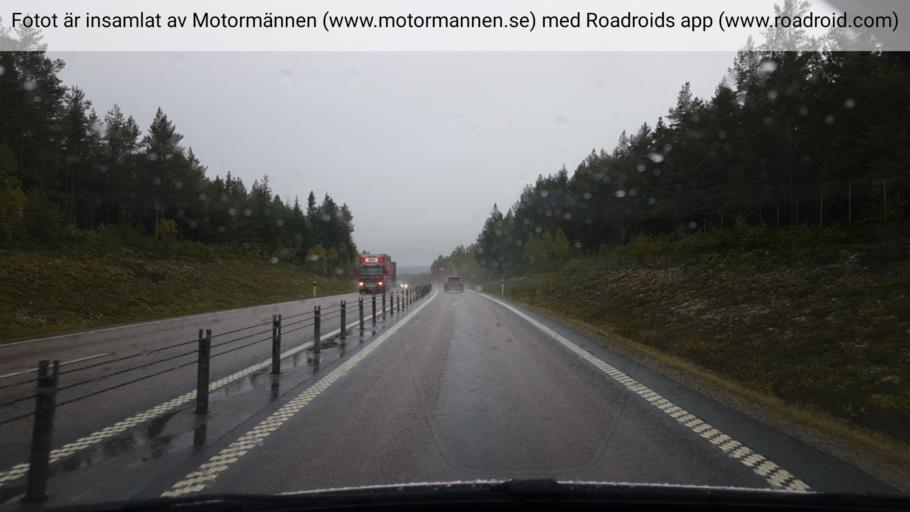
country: SE
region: Gaevleborg
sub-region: Hudiksvalls Kommun
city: Hudiksvall
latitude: 61.7723
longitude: 17.1030
